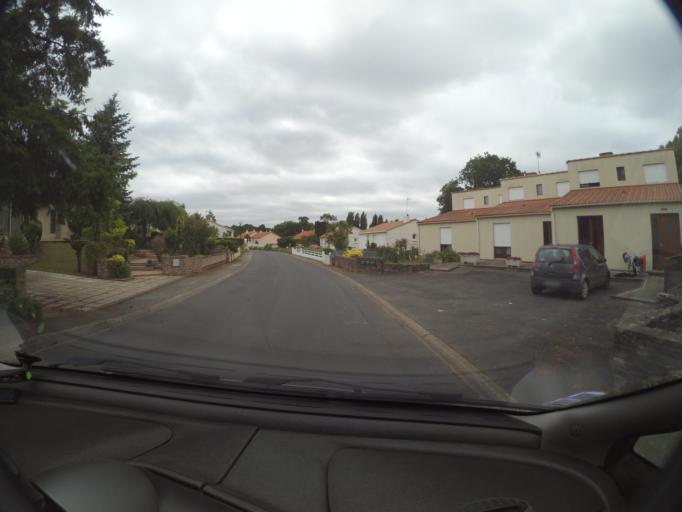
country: FR
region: Pays de la Loire
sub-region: Departement de la Vendee
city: Saint-Hilaire-de-Loulay
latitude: 46.9989
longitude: -1.3336
